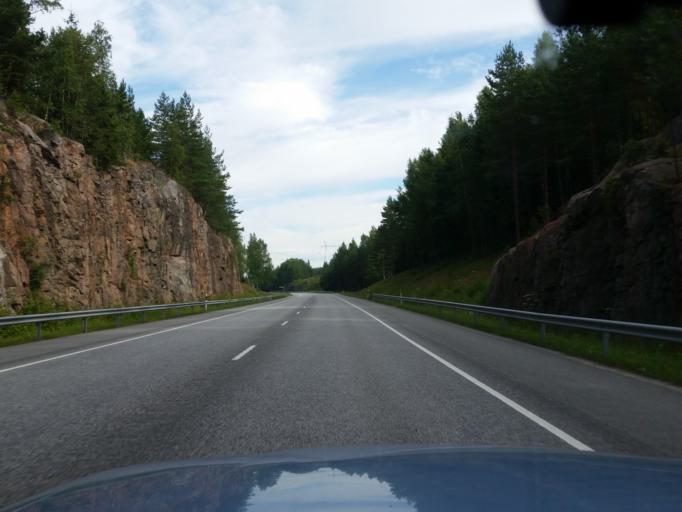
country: FI
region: Uusimaa
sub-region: Raaseporin
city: Karis
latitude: 60.0716
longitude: 23.7775
